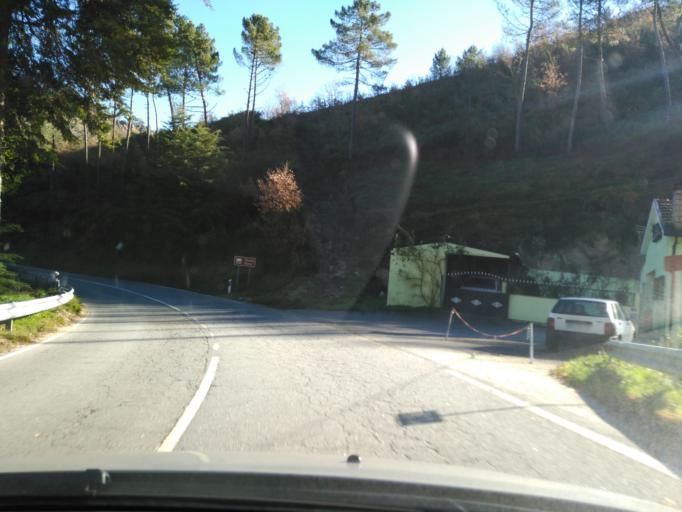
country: PT
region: Braga
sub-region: Cabeceiras de Basto
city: Cabeceiras de Basto
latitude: 41.6683
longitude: -7.9873
